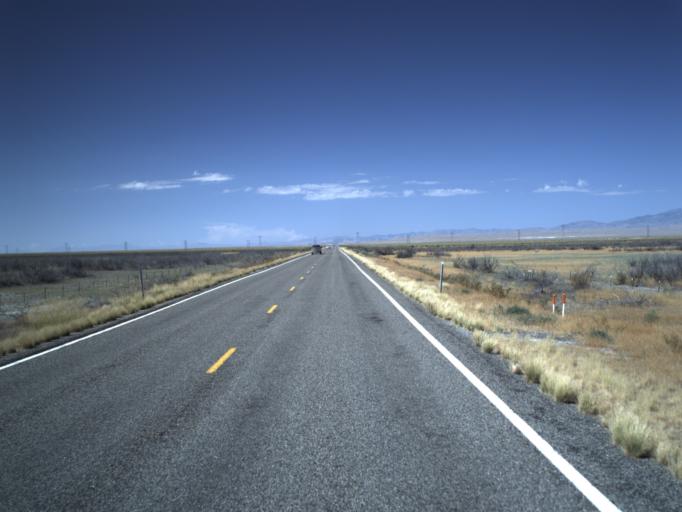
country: US
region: Utah
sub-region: Millard County
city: Delta
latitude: 39.2625
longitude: -112.8766
